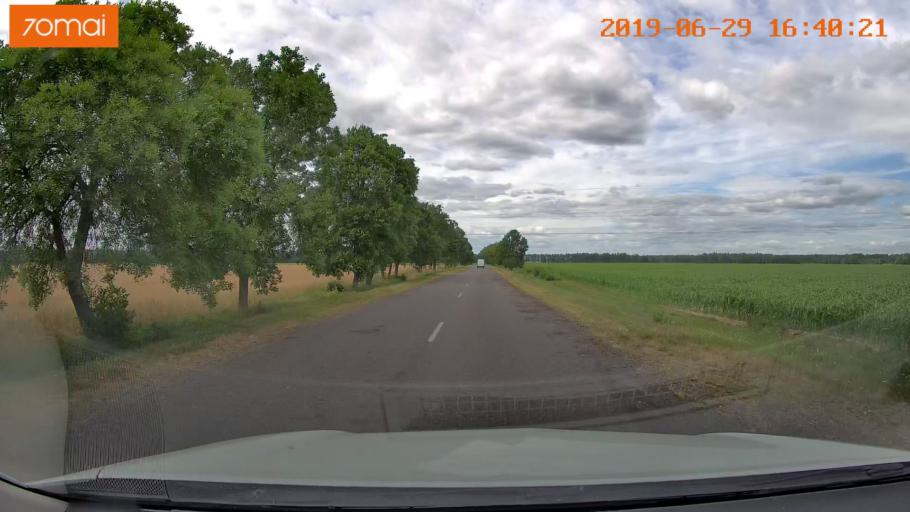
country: BY
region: Brest
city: Luninyets
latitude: 52.2547
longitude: 27.0171
